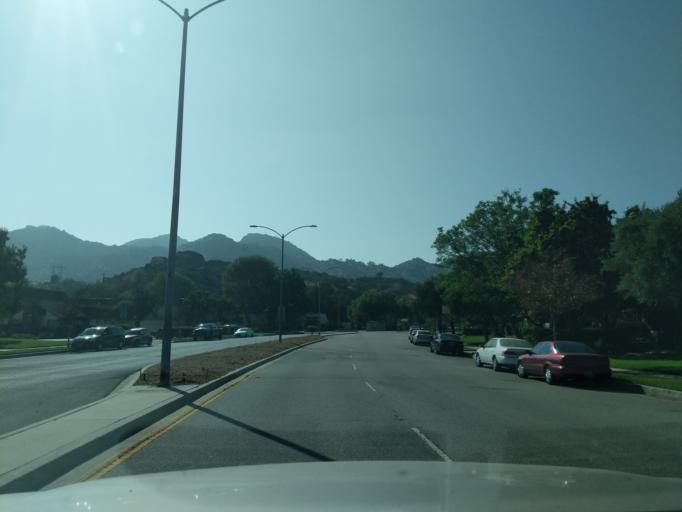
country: US
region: California
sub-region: Los Angeles County
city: Chatsworth
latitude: 34.2574
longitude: -118.6130
